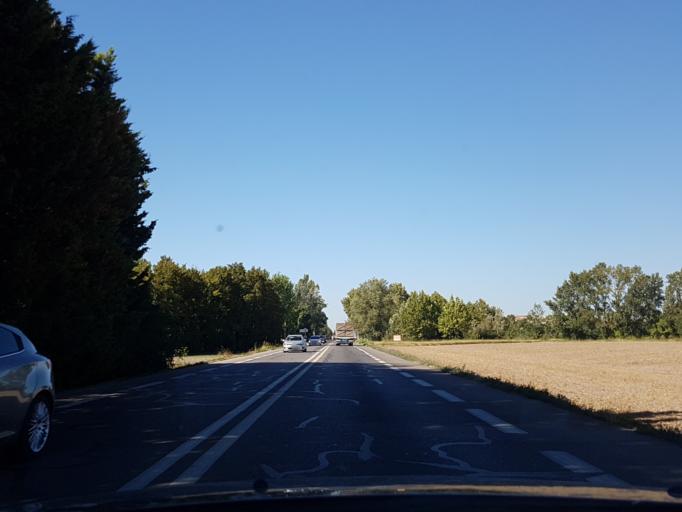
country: FR
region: Provence-Alpes-Cote d'Azur
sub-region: Departement du Vaucluse
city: Velleron
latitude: 43.9479
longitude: 5.0276
